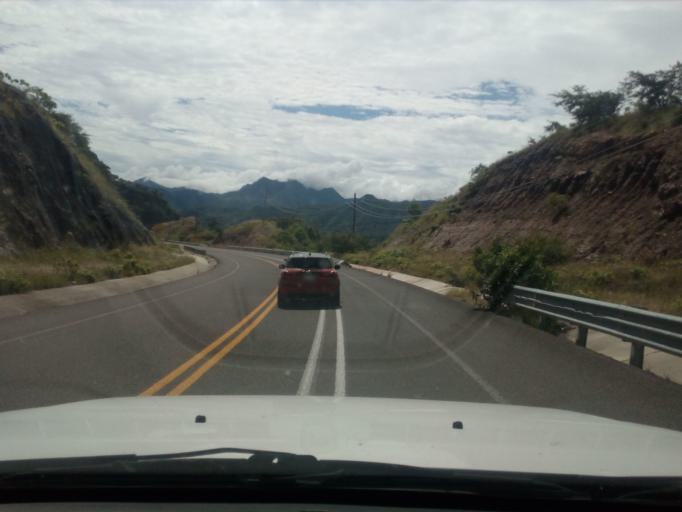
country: MX
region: Durango
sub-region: Pueblo Nuevo
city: La Ciudad
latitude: 23.5603
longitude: -105.7525
